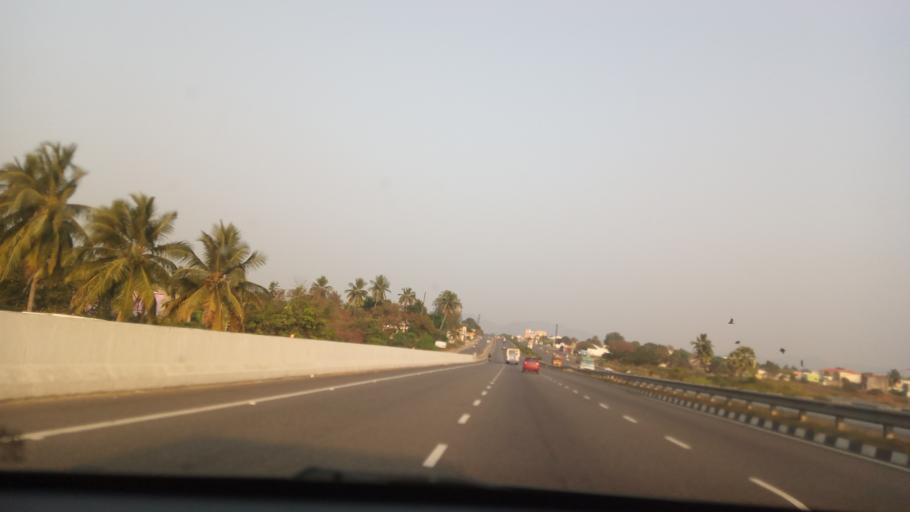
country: IN
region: Tamil Nadu
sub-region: Vellore
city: Vellore
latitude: 12.9150
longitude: 79.0675
